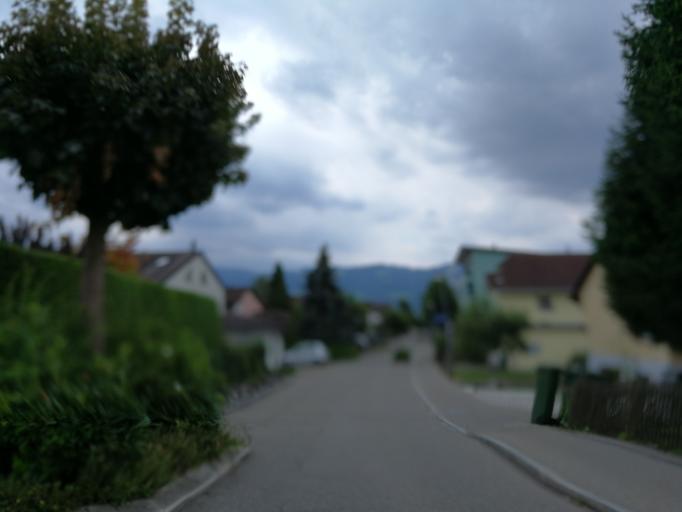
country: CH
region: Saint Gallen
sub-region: Wahlkreis See-Gaster
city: Jona
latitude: 47.2300
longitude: 8.8513
